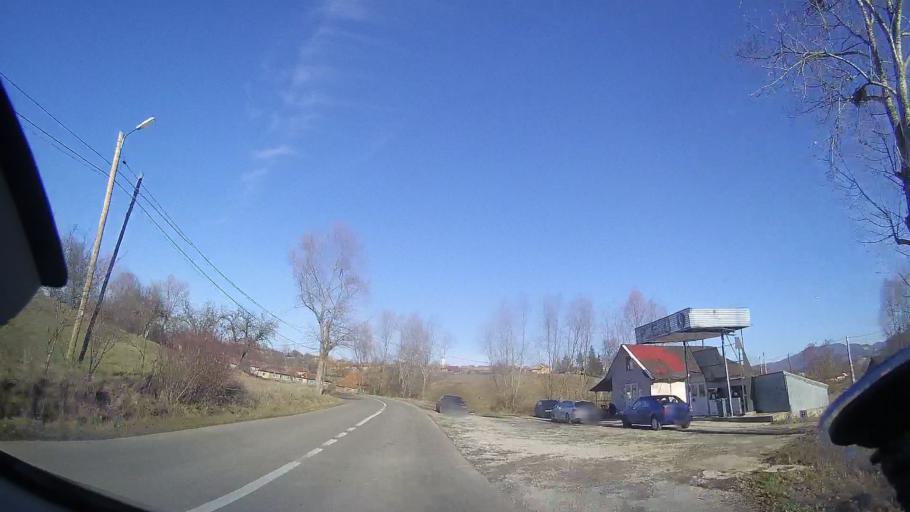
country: RO
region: Bihor
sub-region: Comuna Bratca
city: Beznea
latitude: 46.9515
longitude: 22.6123
